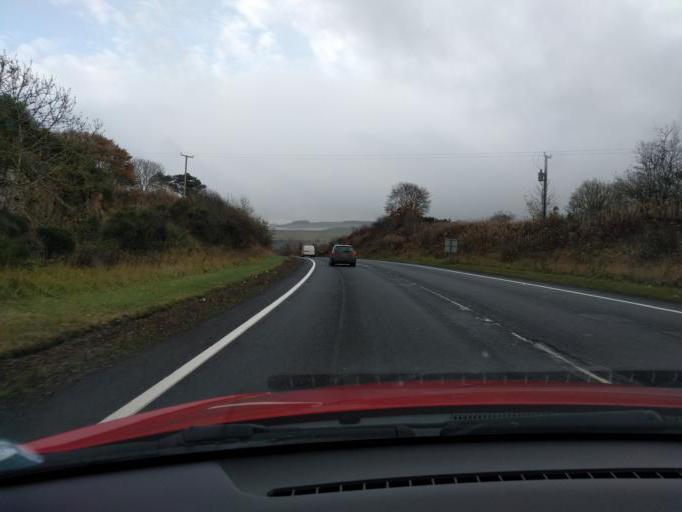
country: GB
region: Scotland
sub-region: The Scottish Borders
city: Chirnside
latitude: 55.8749
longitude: -2.2826
